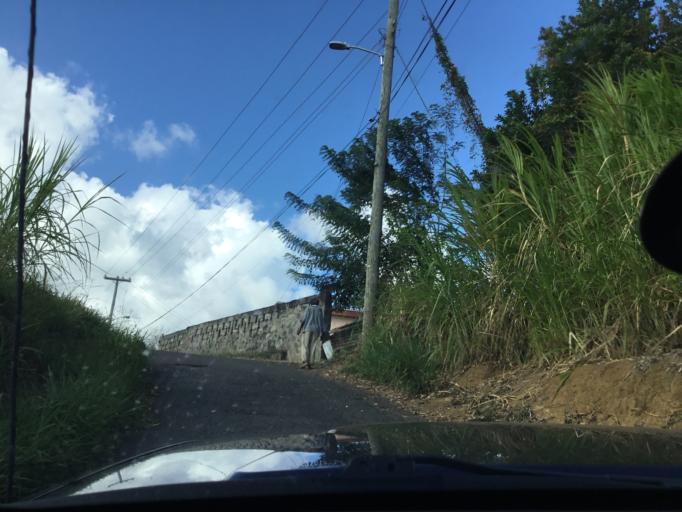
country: VC
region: Saint George
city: Kingstown
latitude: 13.1568
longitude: -61.1777
